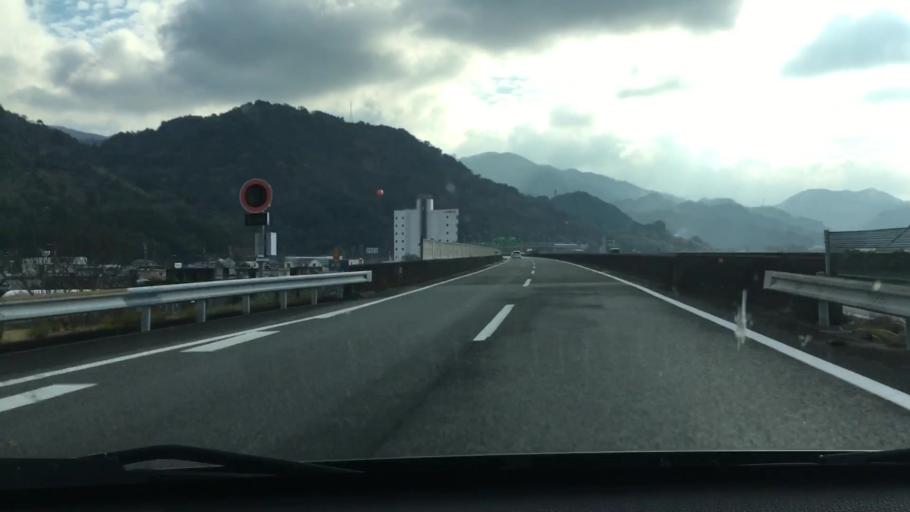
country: JP
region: Kumamoto
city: Yatsushiro
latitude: 32.5100
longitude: 130.6469
